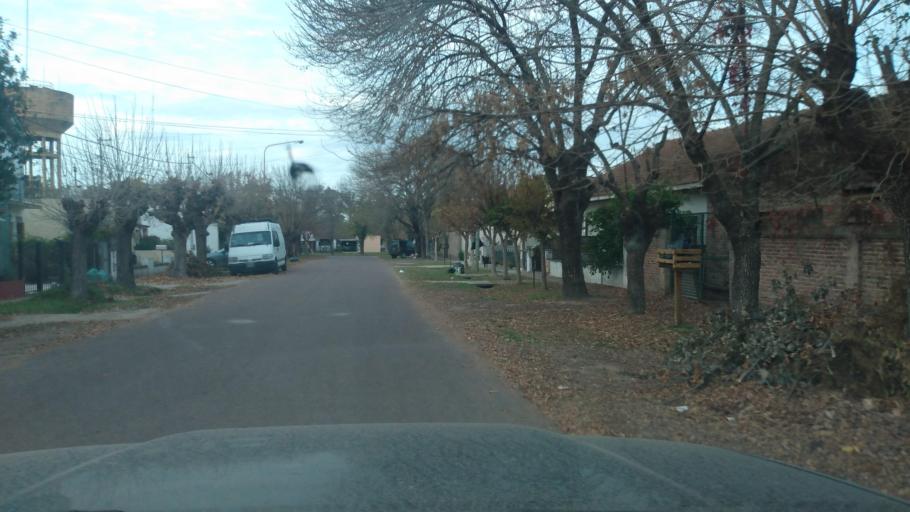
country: AR
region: Buenos Aires
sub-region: Partido de Lujan
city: Lujan
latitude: -34.5990
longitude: -59.1744
